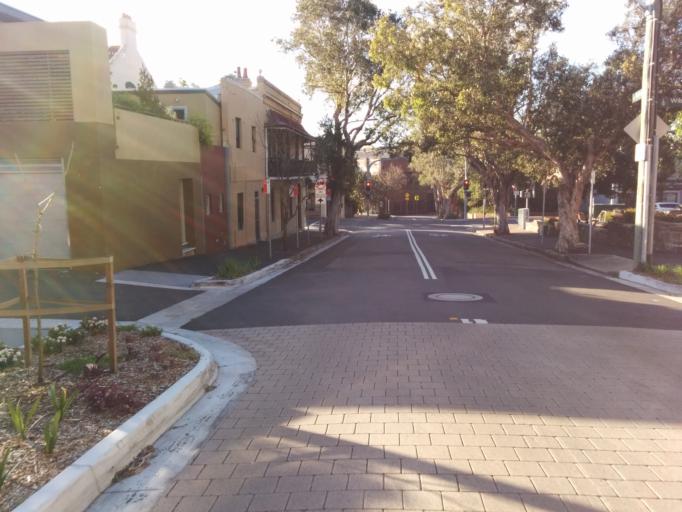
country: AU
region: New South Wales
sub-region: City of Sydney
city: Darlington
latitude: -33.8925
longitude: 151.1941
